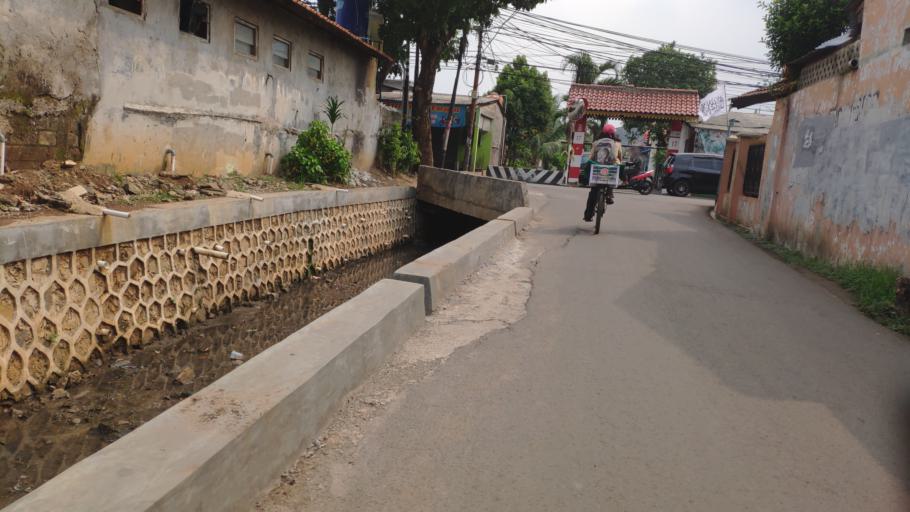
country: ID
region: West Java
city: Depok
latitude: -6.3445
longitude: 106.8149
